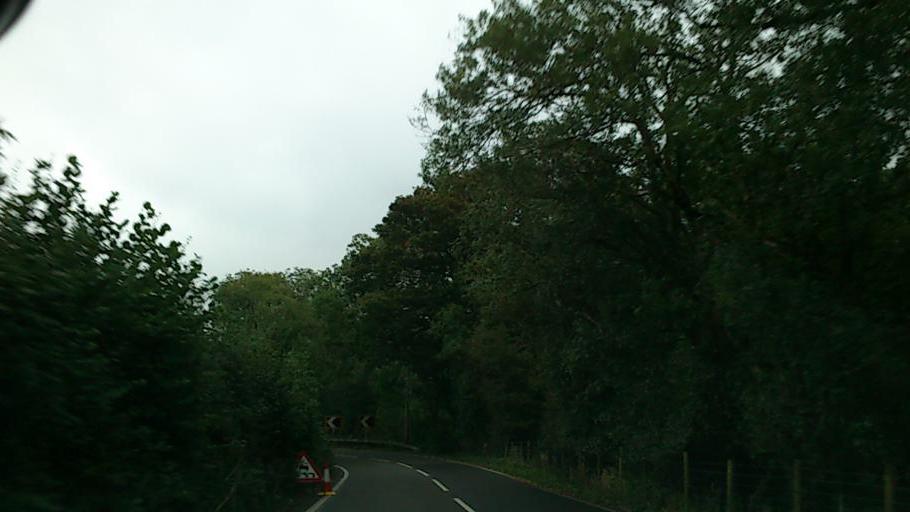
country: GB
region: Wales
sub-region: Gwynedd
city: Bala
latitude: 52.6980
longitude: -3.6283
